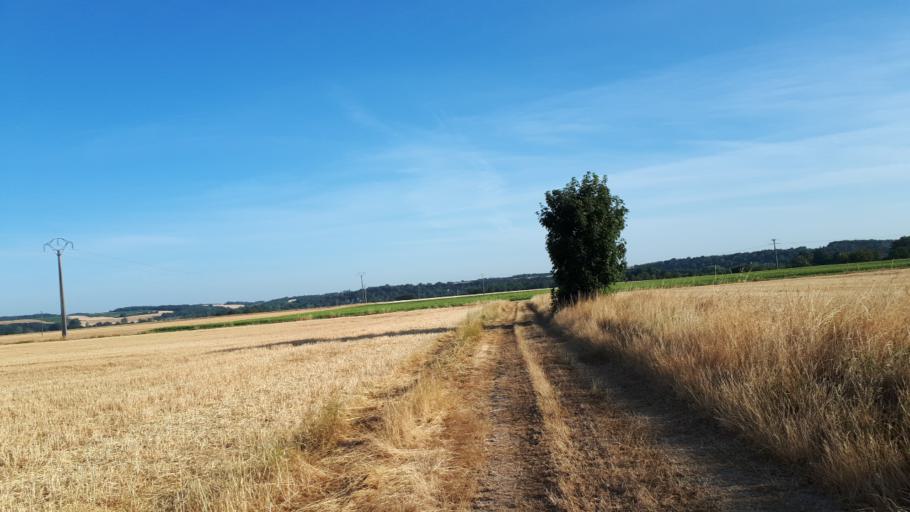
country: FR
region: Centre
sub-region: Departement du Loir-et-Cher
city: Villiers-sur-Loir
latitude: 47.7954
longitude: 0.9782
